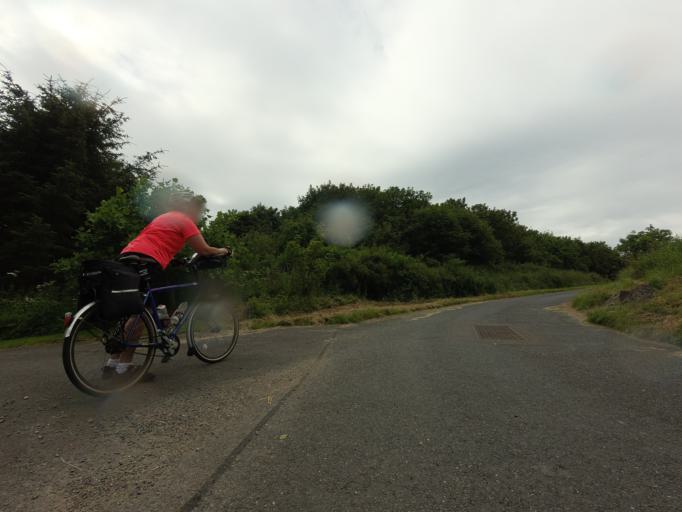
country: GB
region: Scotland
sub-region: Aberdeenshire
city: Portsoy
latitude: 57.6762
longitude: -2.6571
